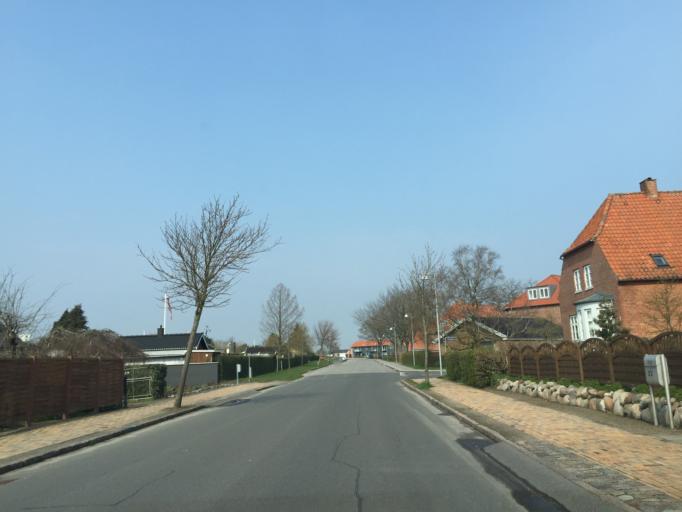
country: DK
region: South Denmark
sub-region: Odense Kommune
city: Odense
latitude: 55.4162
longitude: 10.3921
